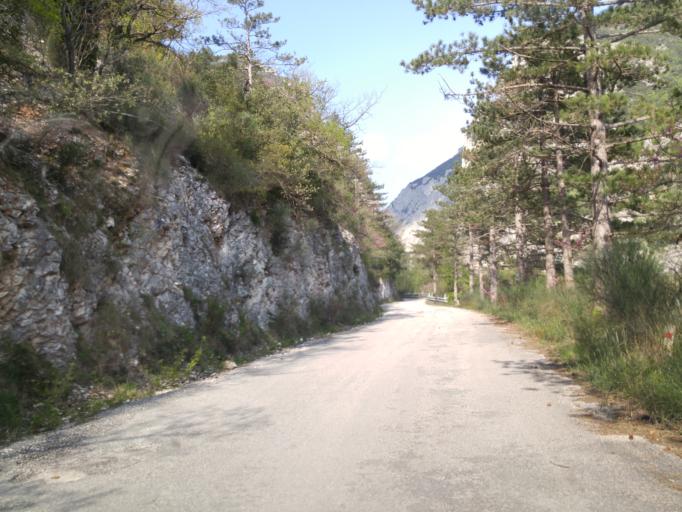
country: IT
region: The Marches
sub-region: Provincia di Pesaro e Urbino
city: Acqualagna
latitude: 43.6391
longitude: 12.7130
